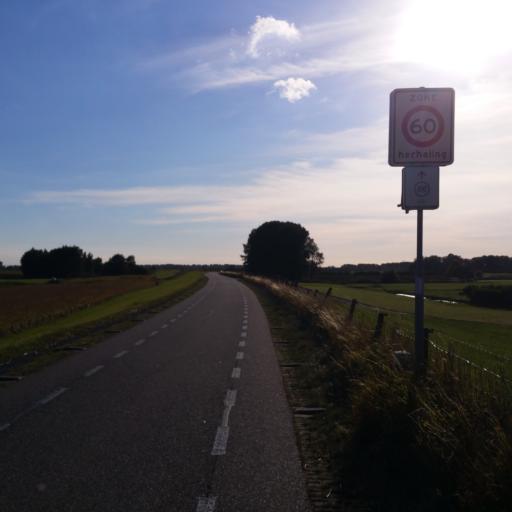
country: NL
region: Utrecht
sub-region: Gemeente IJsselstein
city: IJsselstein
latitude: 51.9842
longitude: 5.0408
